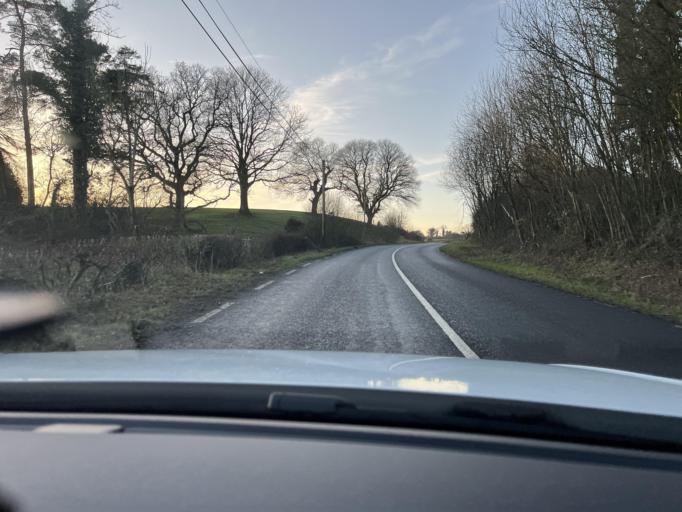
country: IE
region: Ulster
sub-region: An Cabhan
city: Ballyconnell
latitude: 54.0967
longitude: -7.6177
